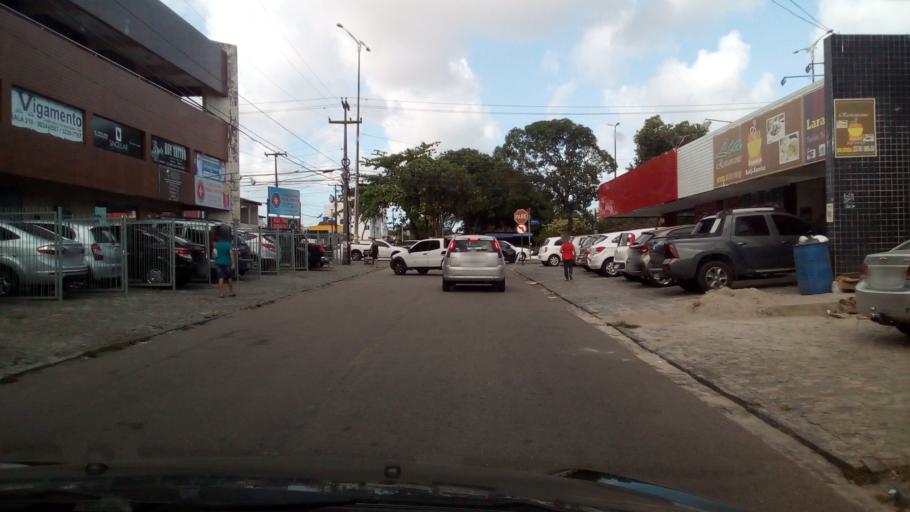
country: BR
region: Paraiba
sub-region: Joao Pessoa
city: Joao Pessoa
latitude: -7.1485
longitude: -34.8446
